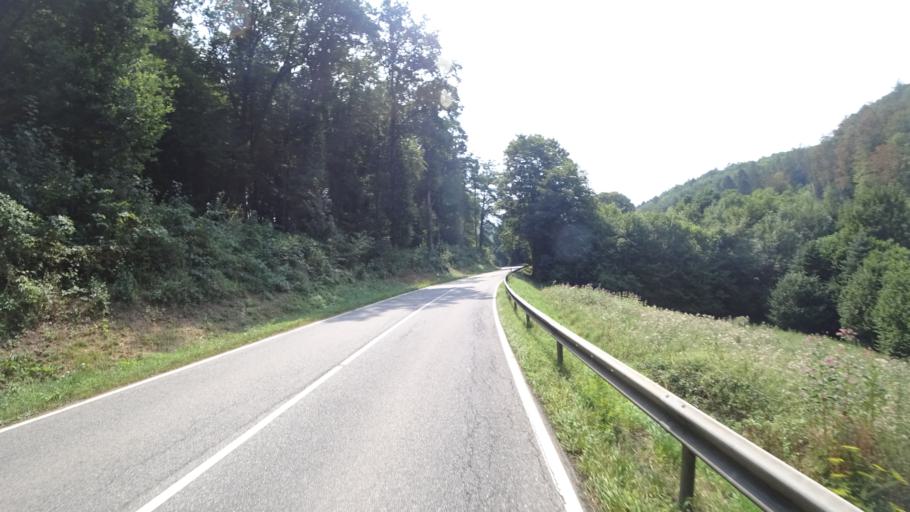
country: DE
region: Rheinland-Pfalz
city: Hohr-Grenzhausen
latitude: 50.4283
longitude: 7.6507
